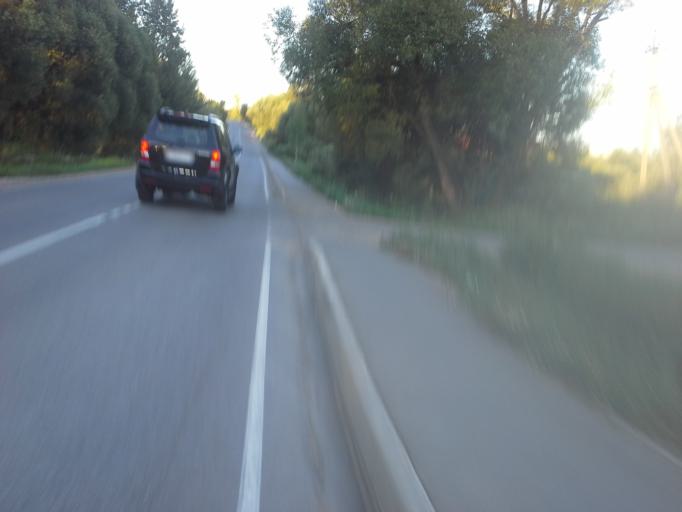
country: RU
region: Moskovskaya
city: Selyatino
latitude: 55.5186
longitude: 36.9556
